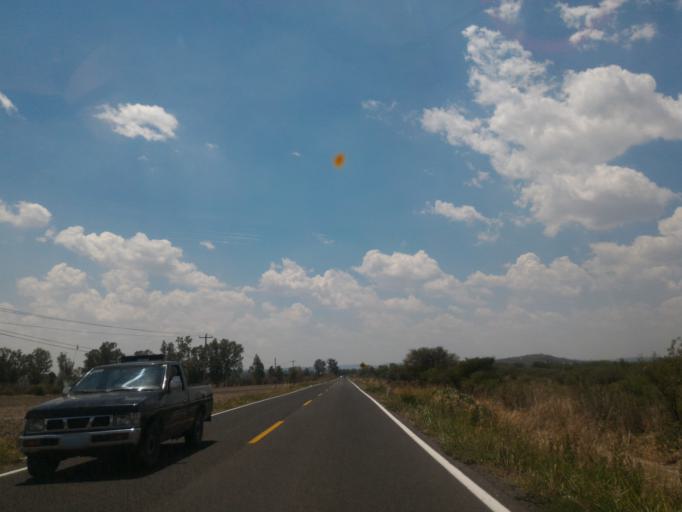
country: MX
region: Guanajuato
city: Ciudad Manuel Doblado
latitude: 20.7799
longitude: -101.9782
